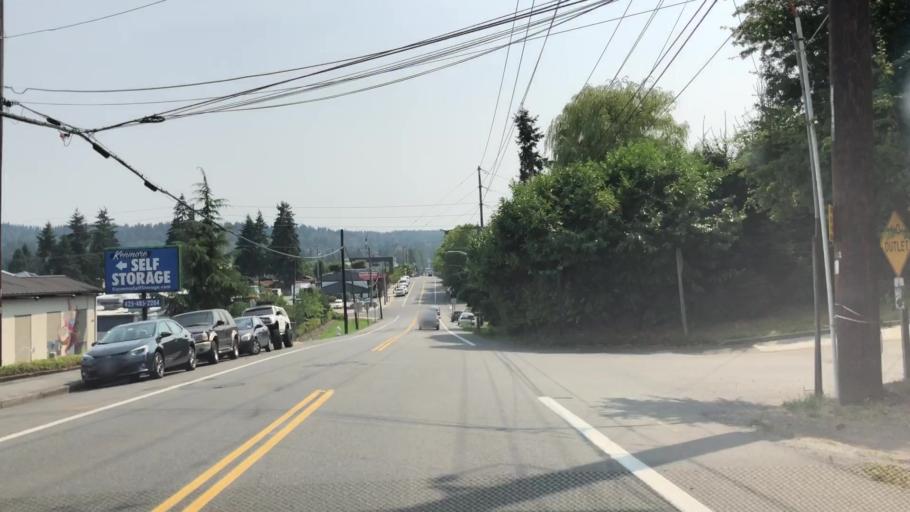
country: US
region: Washington
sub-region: King County
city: Kenmore
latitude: 47.7640
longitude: -122.2496
